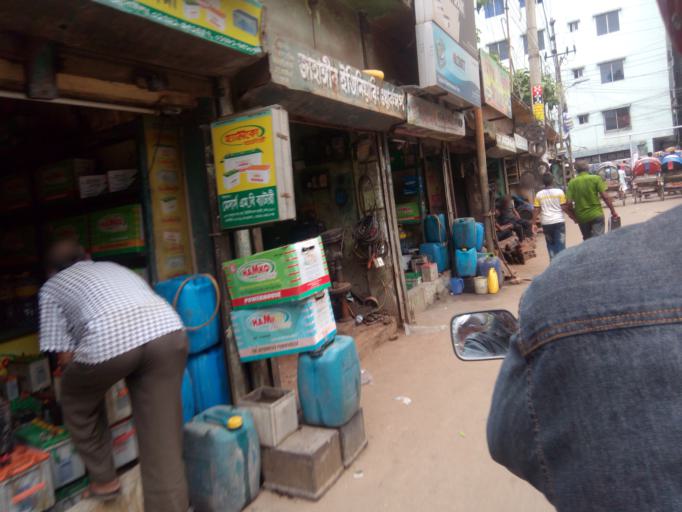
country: BD
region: Dhaka
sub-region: Dhaka
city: Dhaka
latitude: 23.7101
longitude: 90.4128
